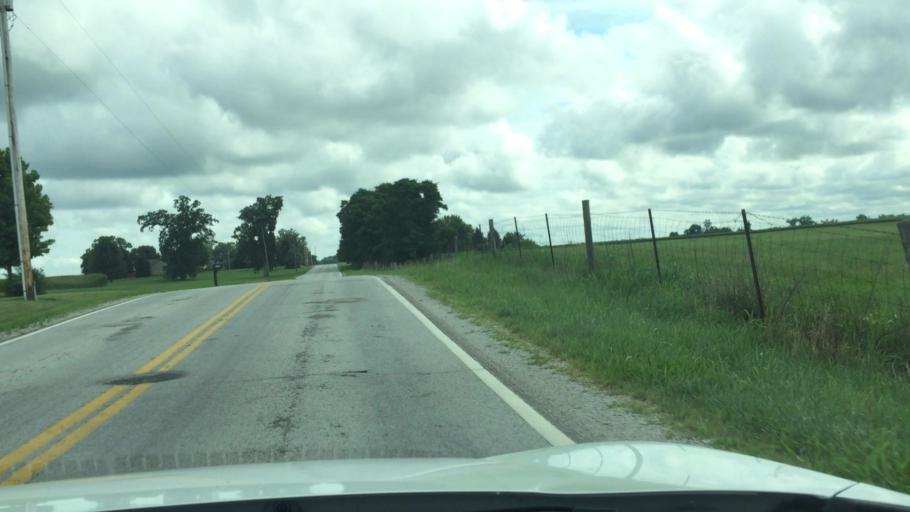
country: US
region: Ohio
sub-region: Clark County
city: Northridge
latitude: 39.9591
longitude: -83.6800
